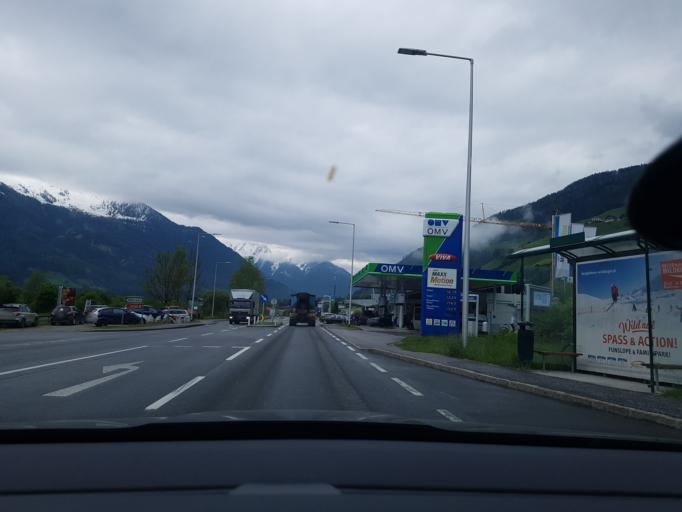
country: AT
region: Salzburg
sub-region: Politischer Bezirk Zell am See
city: Bramberg am Wildkogel
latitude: 47.2680
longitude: 12.3383
